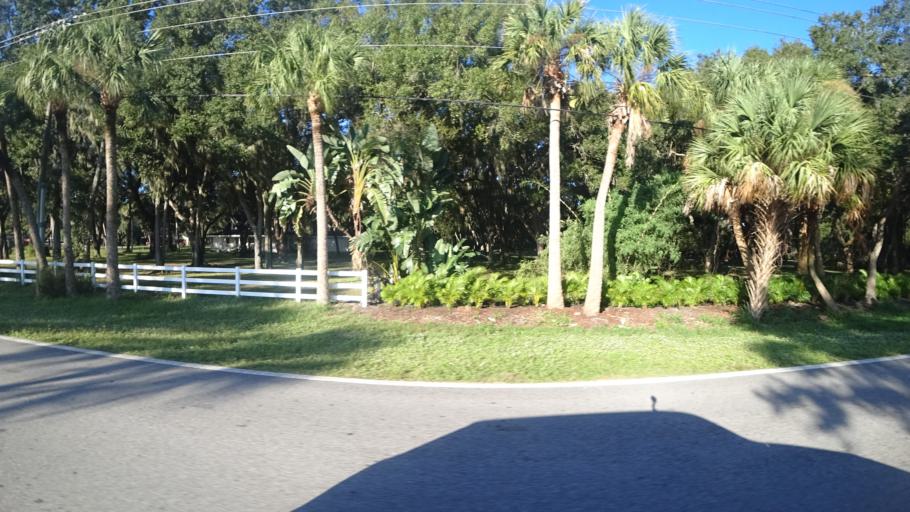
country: US
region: Florida
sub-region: Manatee County
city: Memphis
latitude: 27.5698
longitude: -82.5565
